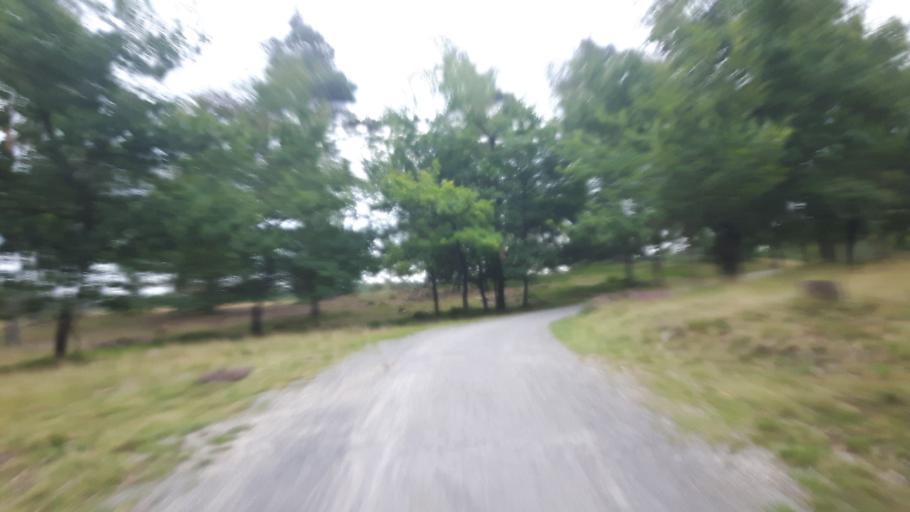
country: NL
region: Drenthe
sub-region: Gemeente Westerveld
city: Dwingeloo
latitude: 52.9449
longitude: 6.3084
